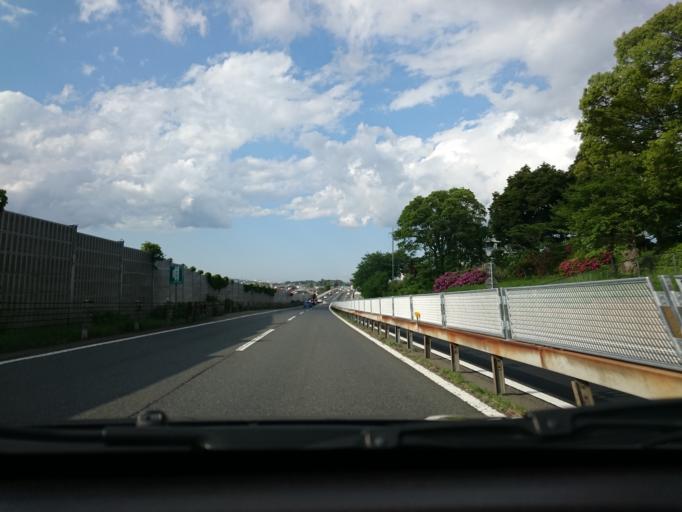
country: JP
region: Kanagawa
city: Isehara
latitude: 35.3543
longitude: 139.2998
